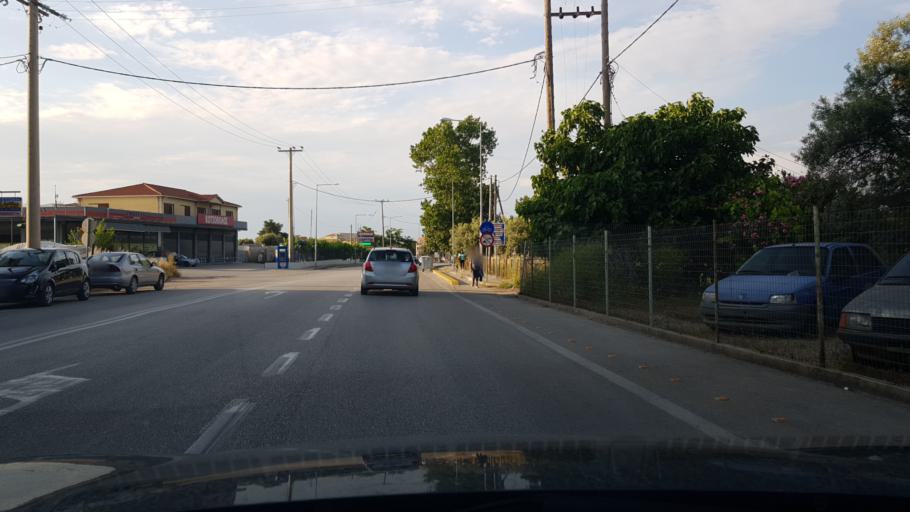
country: GR
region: Ionian Islands
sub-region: Lefkada
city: Lefkada
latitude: 38.8223
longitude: 20.7022
